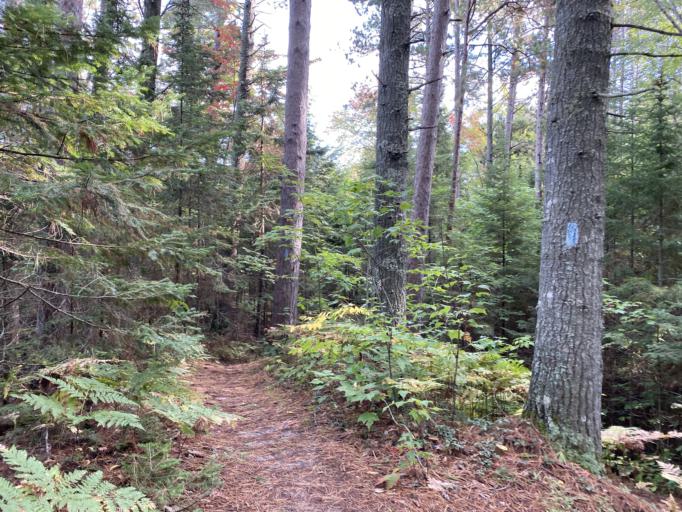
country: US
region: Michigan
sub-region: Mackinac County
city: Saint Ignace
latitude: 45.7424
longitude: -84.8861
